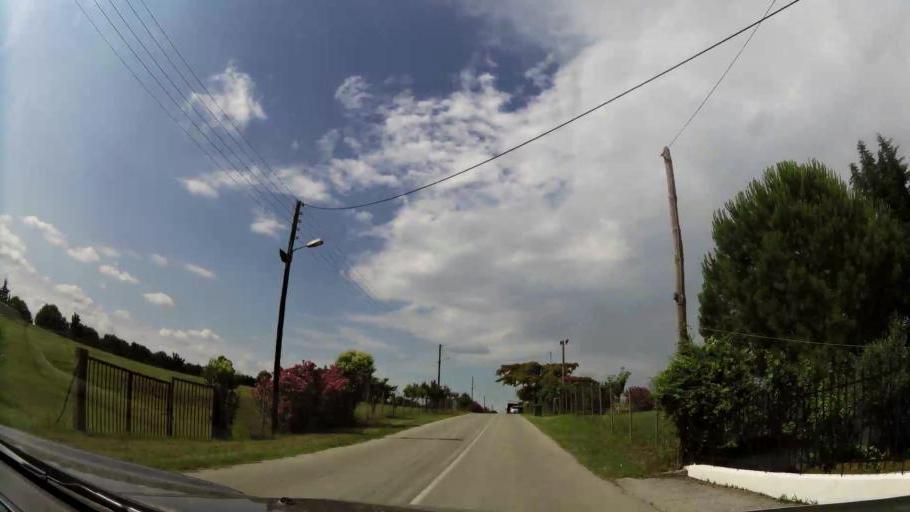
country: GR
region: Central Macedonia
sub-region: Nomos Pierias
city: Makrygialos
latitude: 40.3969
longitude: 22.6168
